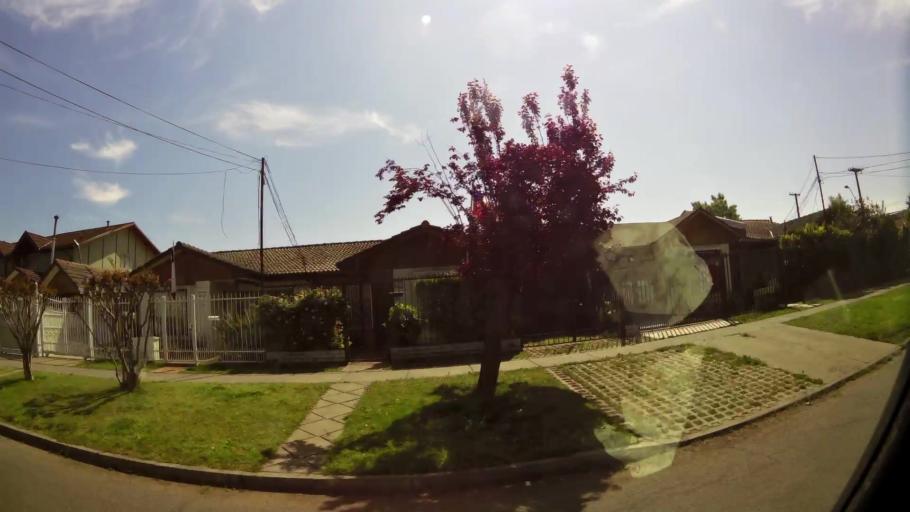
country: CL
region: Santiago Metropolitan
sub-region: Provincia de Santiago
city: Lo Prado
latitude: -33.4670
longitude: -70.7347
